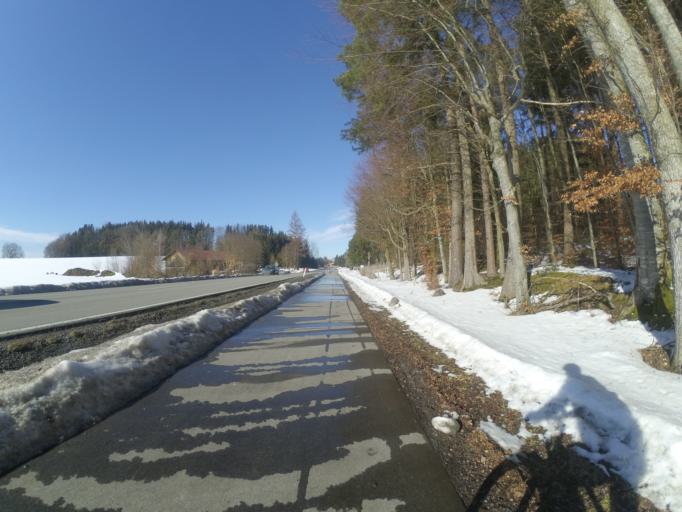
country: DE
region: Bavaria
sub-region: Upper Bavaria
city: Aying
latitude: 47.9564
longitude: 11.7845
